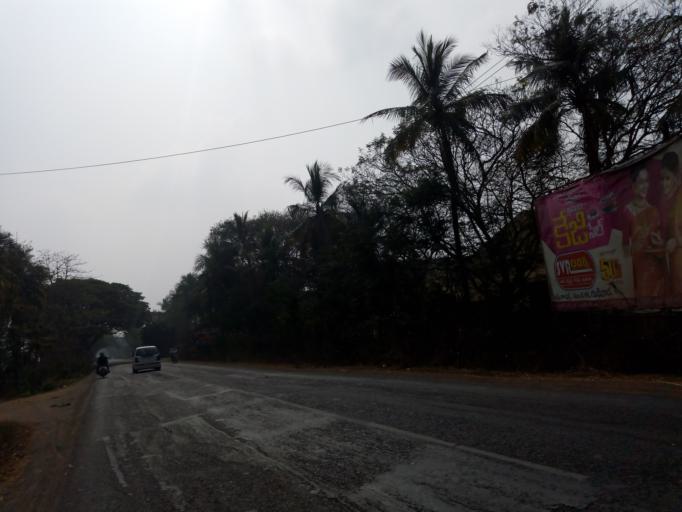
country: IN
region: Andhra Pradesh
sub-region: West Godavari
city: Bhimavaram
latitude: 16.5759
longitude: 81.4803
